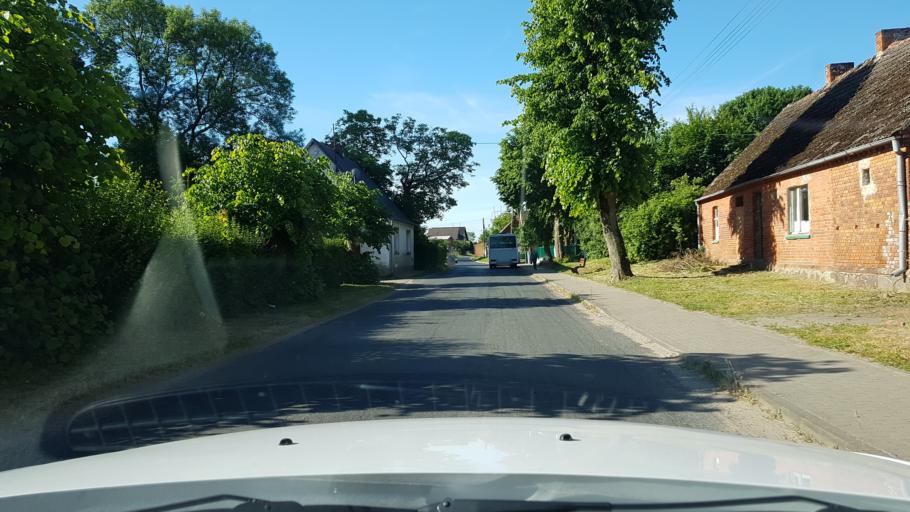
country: PL
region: West Pomeranian Voivodeship
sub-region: Powiat pyrzycki
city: Bielice
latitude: 53.2202
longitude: 14.6099
